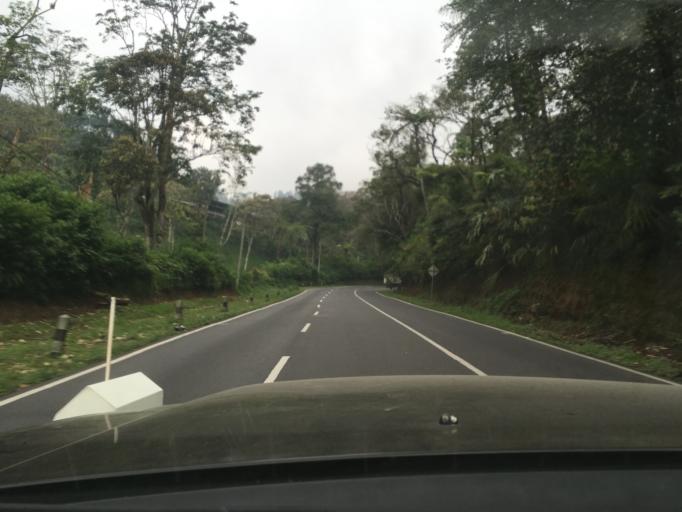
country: ID
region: West Java
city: Lembang
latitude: -6.7691
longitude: 107.6373
